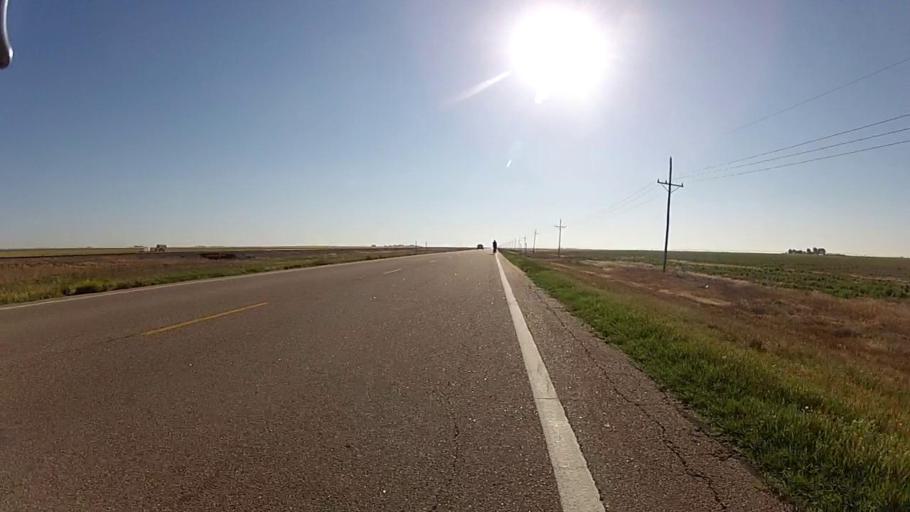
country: US
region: Kansas
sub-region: Haskell County
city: Sublette
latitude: 37.5180
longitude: -100.7193
